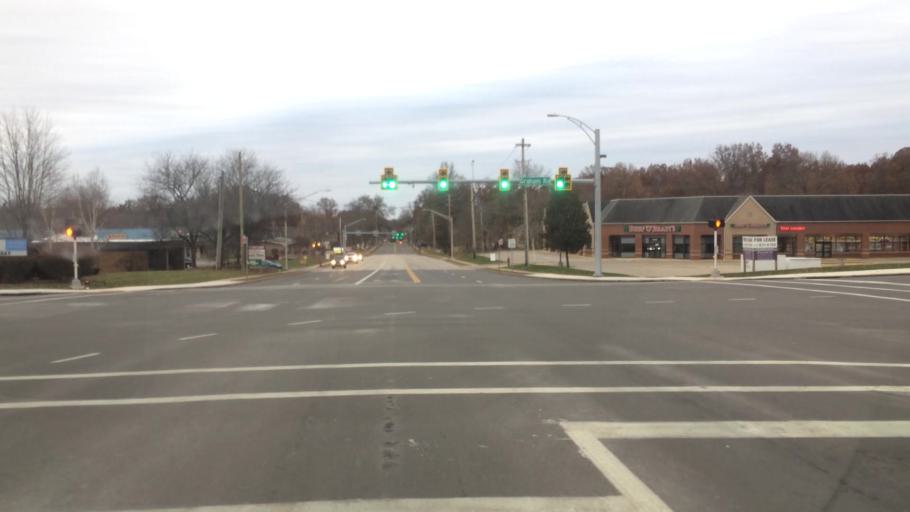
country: US
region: Ohio
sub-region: Summit County
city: Stow
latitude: 41.1669
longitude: -81.4404
